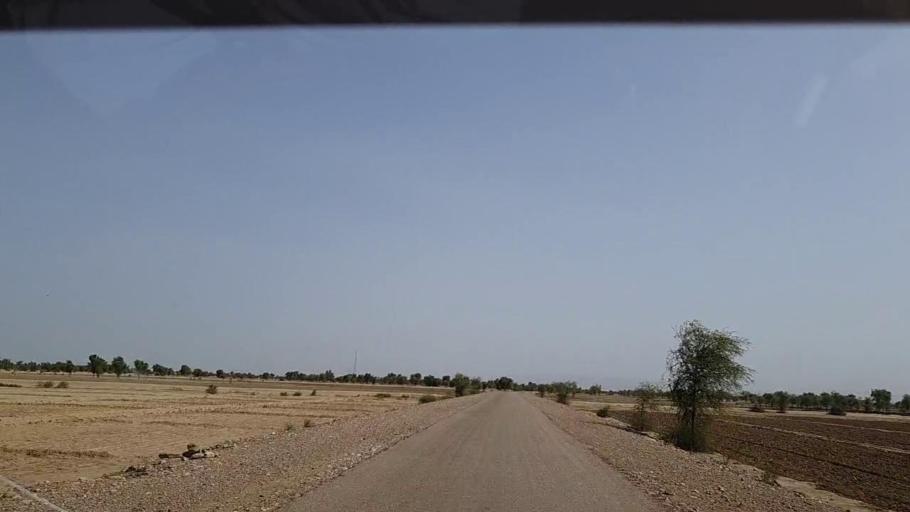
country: PK
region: Sindh
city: Johi
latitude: 26.6514
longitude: 67.5048
